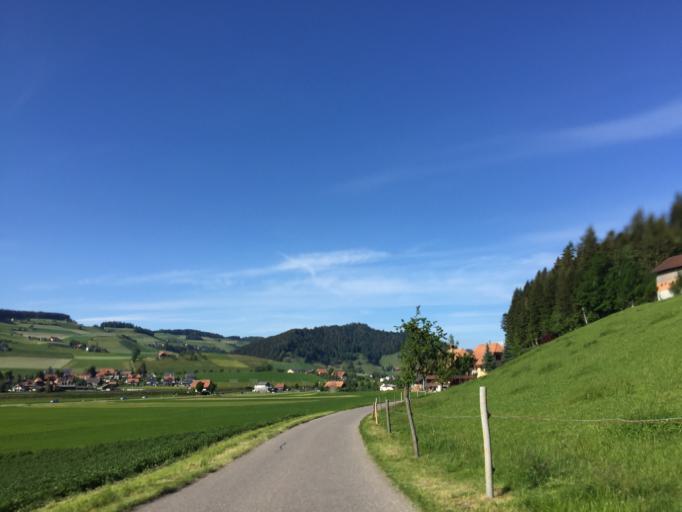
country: CH
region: Bern
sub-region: Bern-Mittelland District
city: Zaziwil
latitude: 46.8871
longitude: 7.6446
